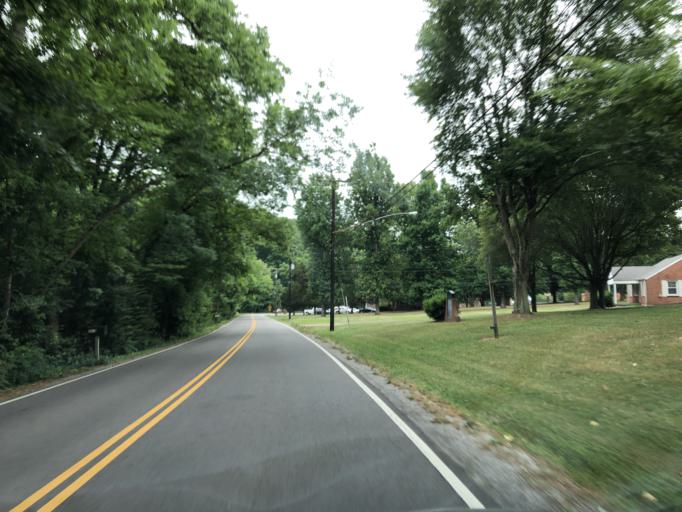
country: US
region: Tennessee
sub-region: Davidson County
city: Goodlettsville
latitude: 36.2899
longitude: -86.7799
